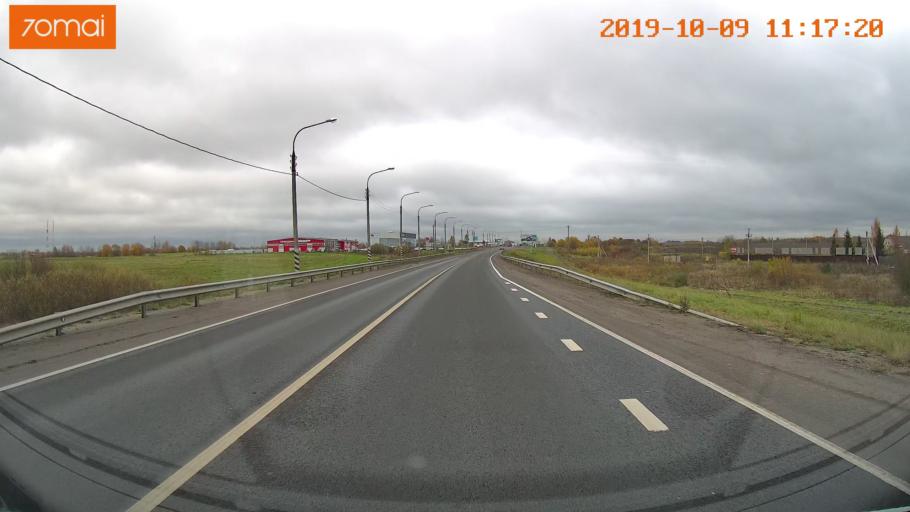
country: RU
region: Vologda
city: Vologda
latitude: 59.1748
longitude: 39.8974
